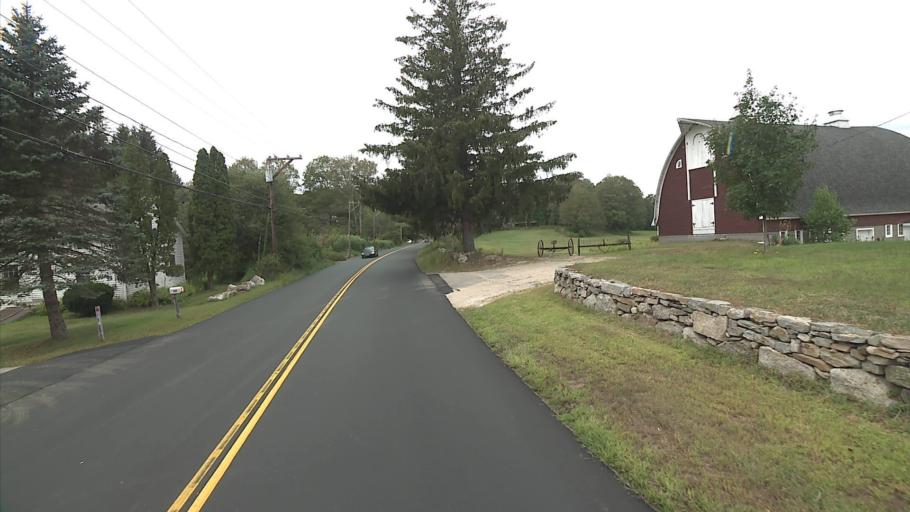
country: US
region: Connecticut
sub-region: New London County
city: Colchester
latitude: 41.5973
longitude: -72.3420
